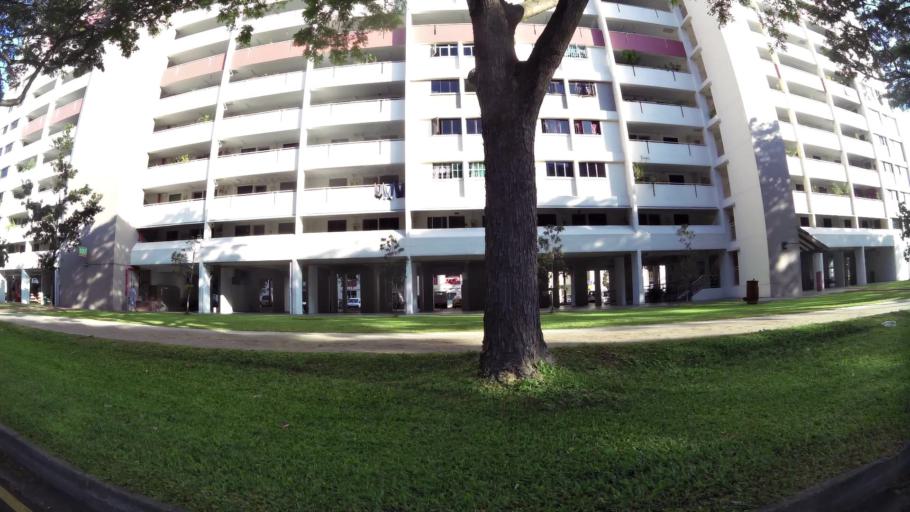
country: SG
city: Singapore
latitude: 1.3320
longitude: 103.9364
